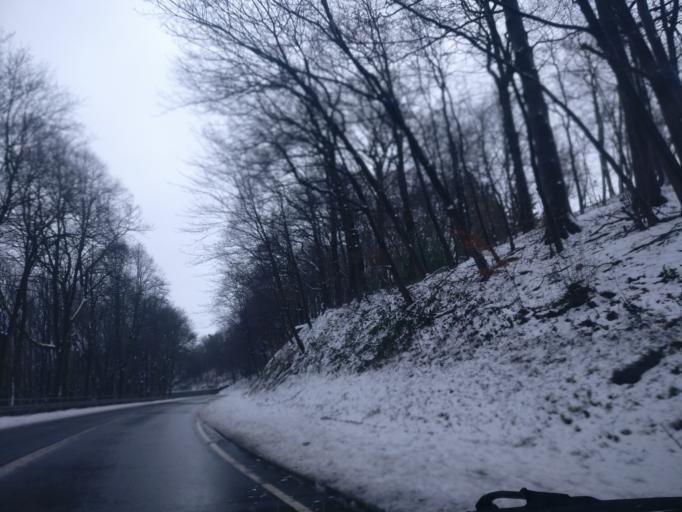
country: DE
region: North Rhine-Westphalia
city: Huckeswagen
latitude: 51.1884
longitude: 7.2808
